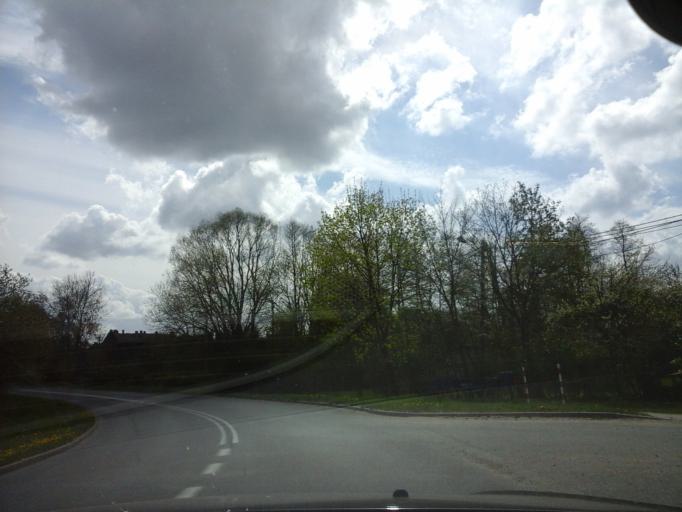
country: PL
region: West Pomeranian Voivodeship
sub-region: Powiat stargardzki
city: Suchan
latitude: 53.2296
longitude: 15.2976
